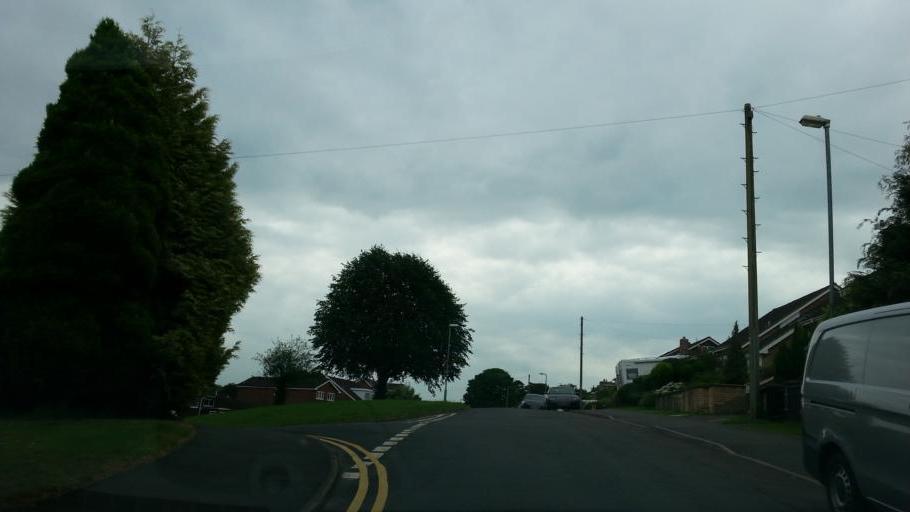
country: GB
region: England
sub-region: Worcestershire
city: Barnt Green
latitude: 52.3889
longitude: -2.0224
